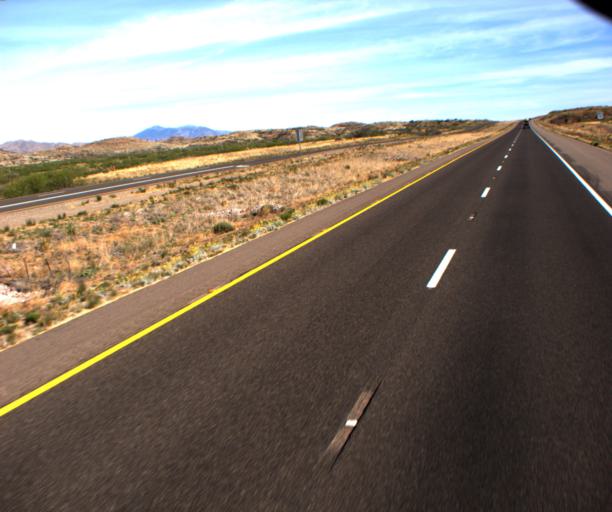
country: US
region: Arizona
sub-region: Cochise County
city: Willcox
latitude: 32.4350
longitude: -109.6633
